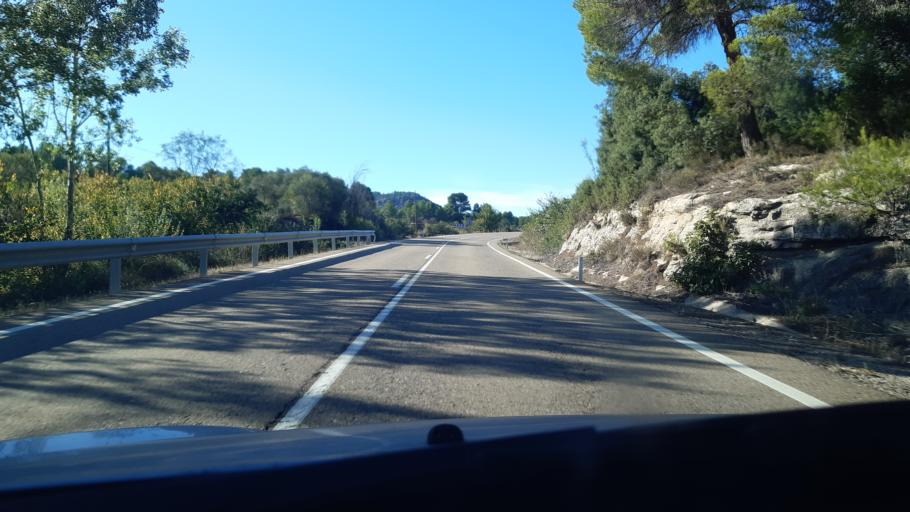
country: ES
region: Aragon
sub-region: Provincia de Teruel
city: Torre del Compte
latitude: 40.9063
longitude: 0.0891
